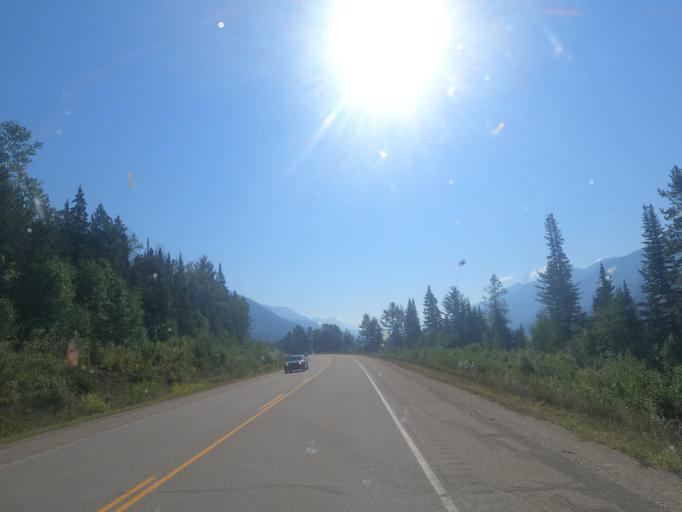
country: CA
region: Alberta
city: Jasper Park Lodge
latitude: 52.9737
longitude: -118.9556
